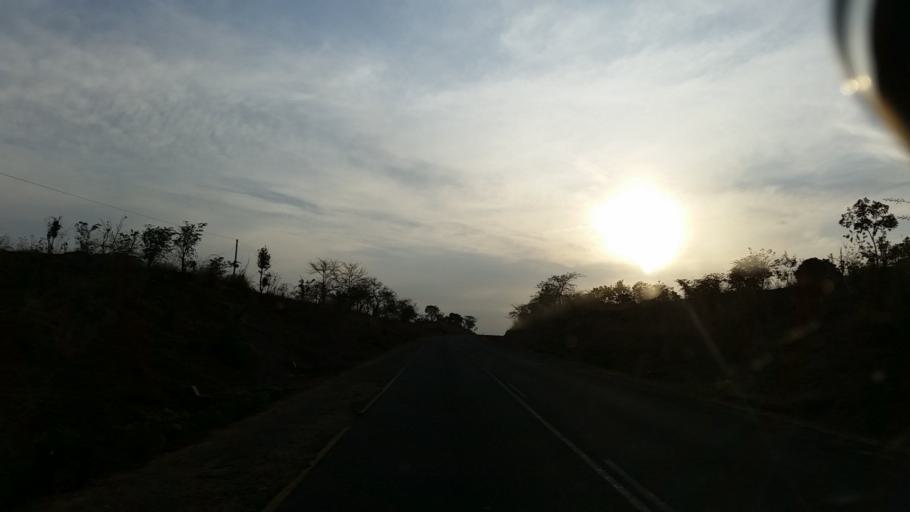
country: MW
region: Central Region
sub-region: Salima District
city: Salima
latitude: -13.7652
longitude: 34.1985
